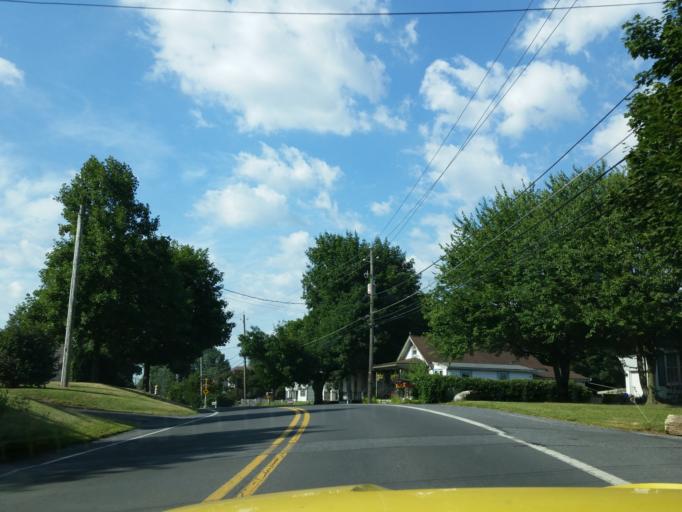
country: US
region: Pennsylvania
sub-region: Lebanon County
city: Sand Hill
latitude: 40.3682
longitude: -76.4160
